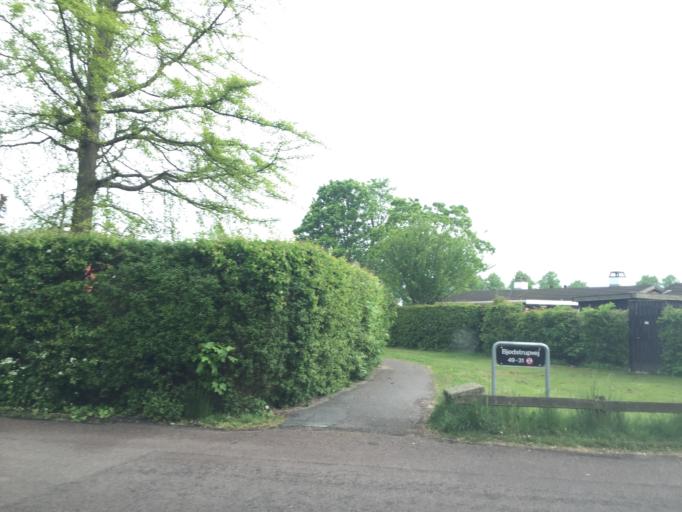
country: DK
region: Capital Region
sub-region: Rodovre Kommune
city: Rodovre
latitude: 55.6820
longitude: 12.4449
